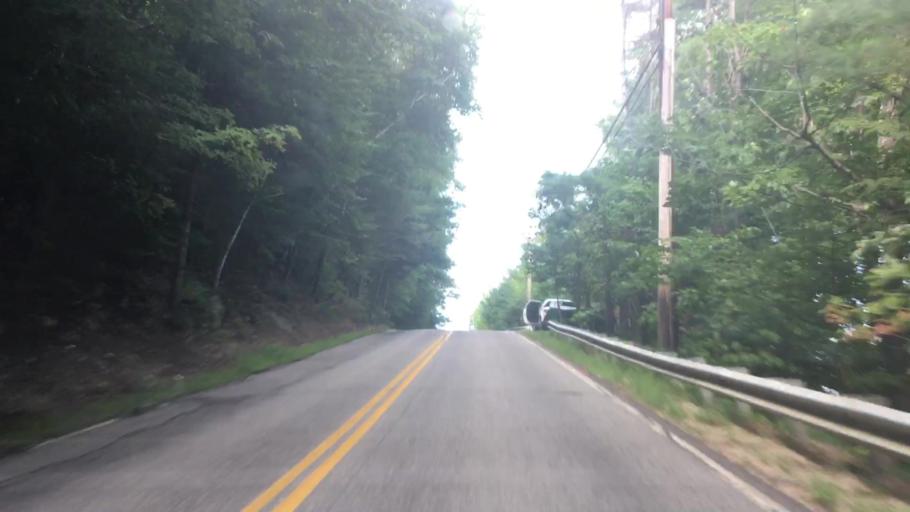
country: US
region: Maine
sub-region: Oxford County
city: Oxford
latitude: 44.1038
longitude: -70.5092
